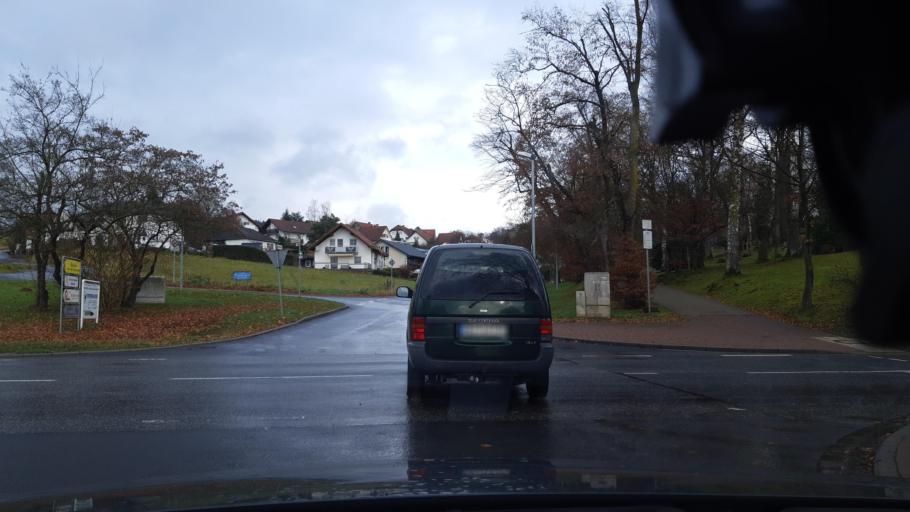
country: DE
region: Hesse
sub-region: Regierungsbezirk Kassel
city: Niederaula
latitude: 50.8046
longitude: 9.5969
